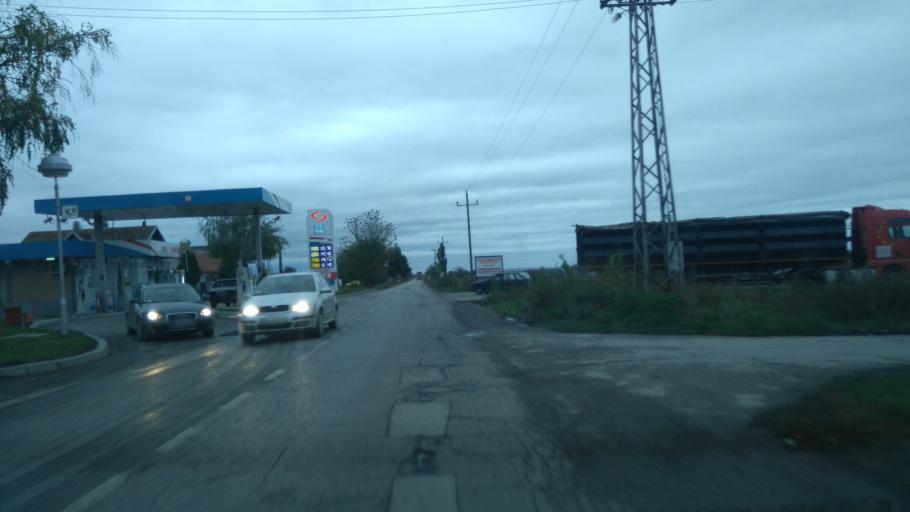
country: RS
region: Autonomna Pokrajina Vojvodina
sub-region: Juznobacki Okrug
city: Durdevo
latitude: 45.3168
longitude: 20.0680
